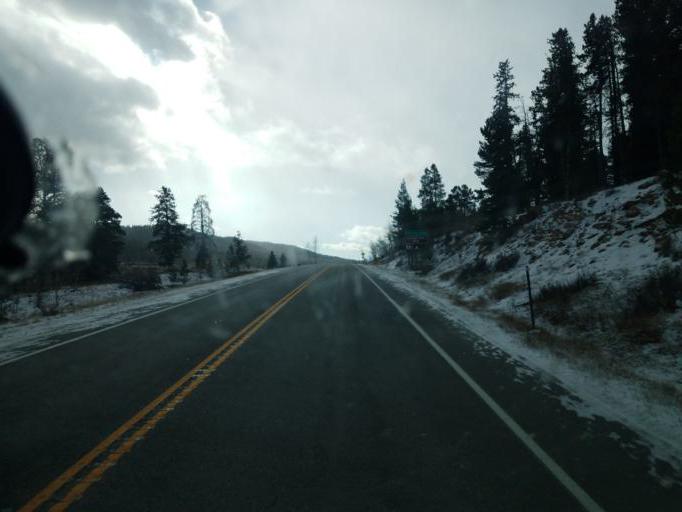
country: US
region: Colorado
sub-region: Summit County
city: Breckenridge
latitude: 39.4147
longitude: -105.7603
